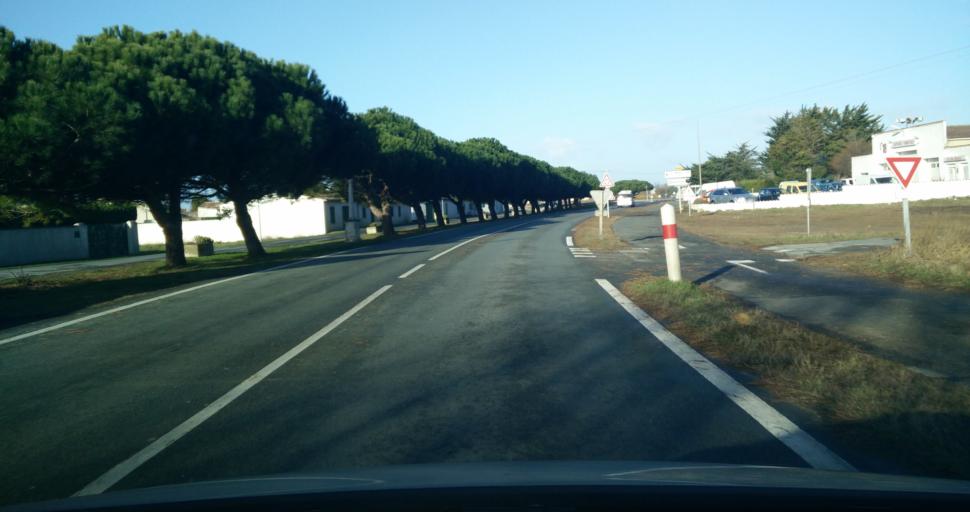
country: FR
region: Poitou-Charentes
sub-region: Departement de la Charente-Maritime
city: Sainte-Marie-de-Re
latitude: 46.1544
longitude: -1.3126
